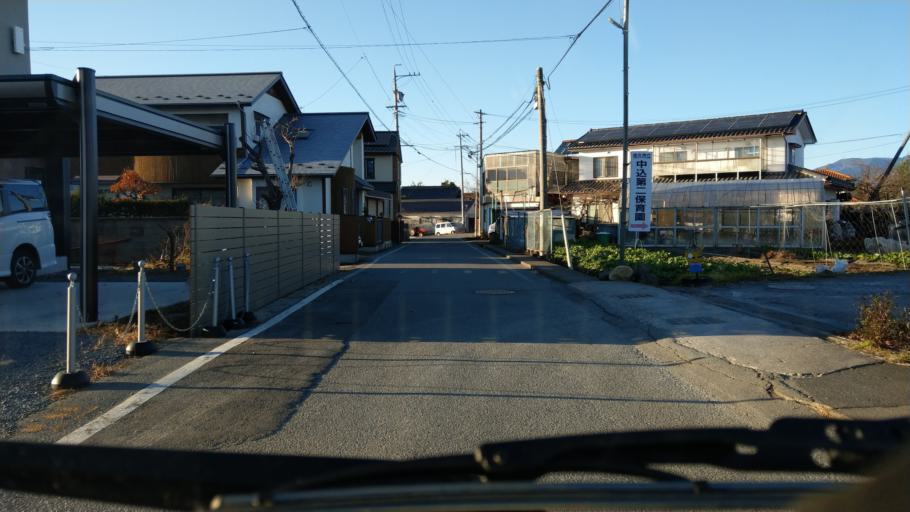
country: JP
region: Nagano
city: Saku
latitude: 36.2384
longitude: 138.4715
